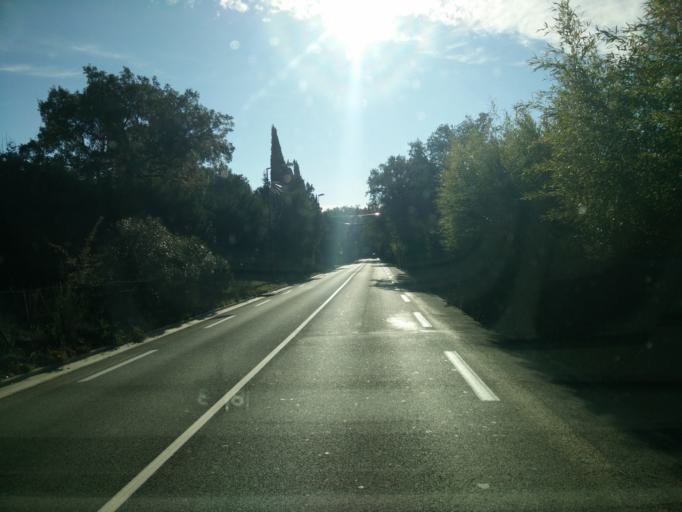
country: FR
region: Provence-Alpes-Cote d'Azur
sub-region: Departement du Var
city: Grimaud
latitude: 43.2716
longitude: 6.5272
